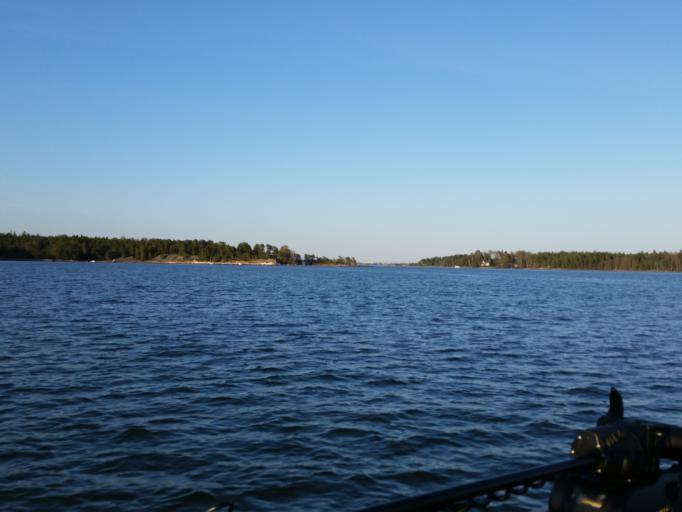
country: FI
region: Uusimaa
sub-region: Helsinki
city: Koukkuniemi
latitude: 60.1344
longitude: 24.7458
